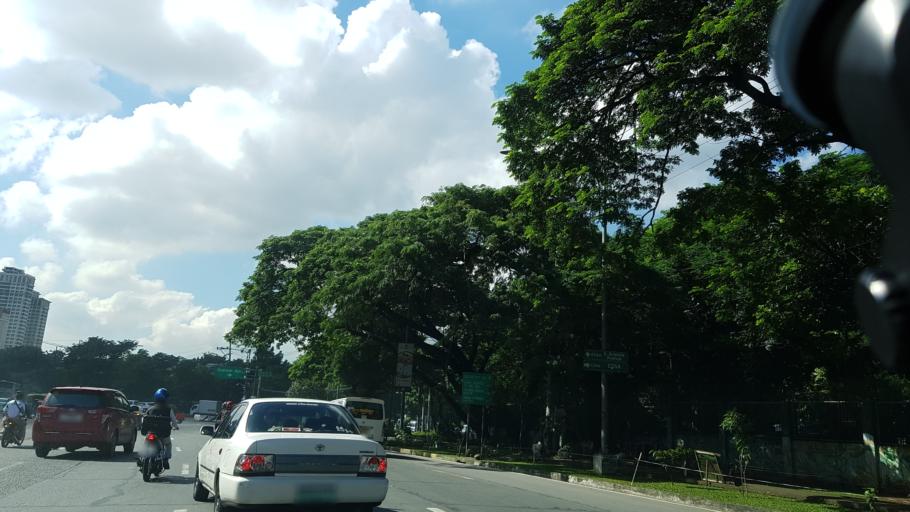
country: PH
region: Metro Manila
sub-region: Quezon City
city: Quezon City
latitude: 14.6510
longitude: 121.0466
